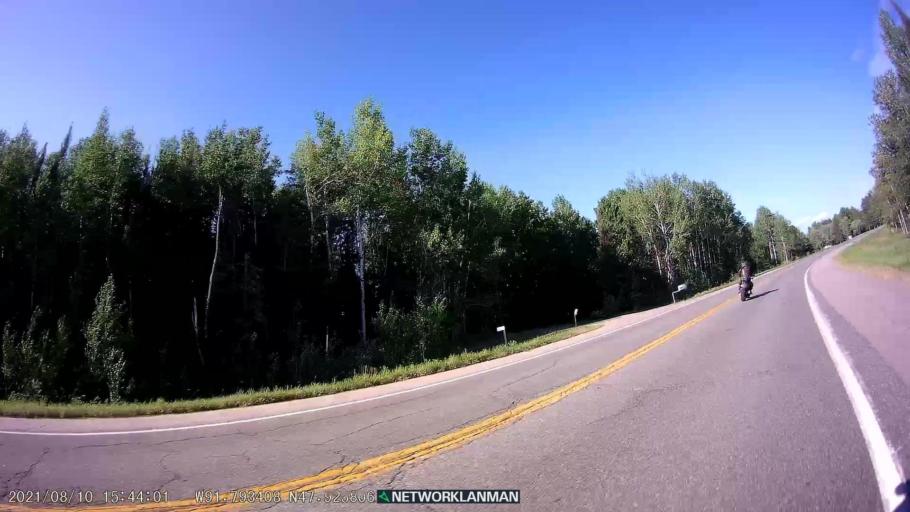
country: US
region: Minnesota
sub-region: Saint Louis County
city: Ely
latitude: 47.9261
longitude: -91.7929
